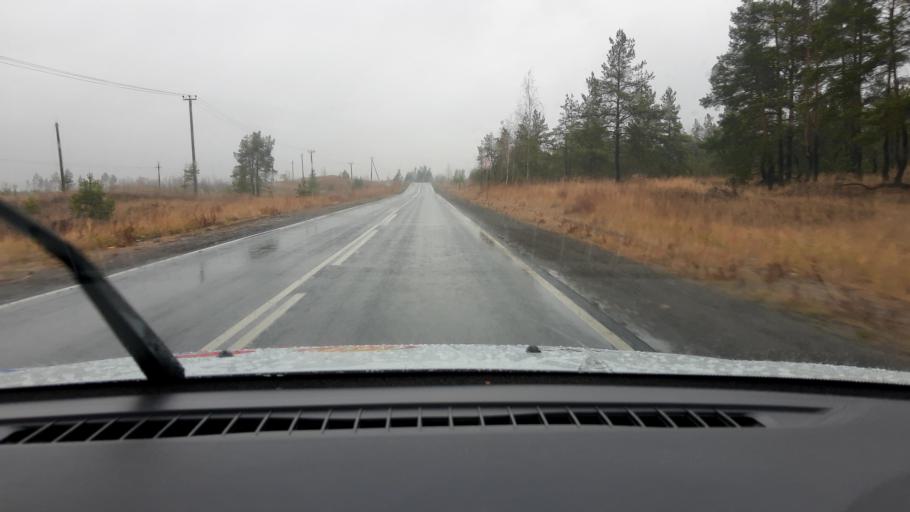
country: RU
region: Nizjnij Novgorod
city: Babino
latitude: 56.2719
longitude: 43.5924
